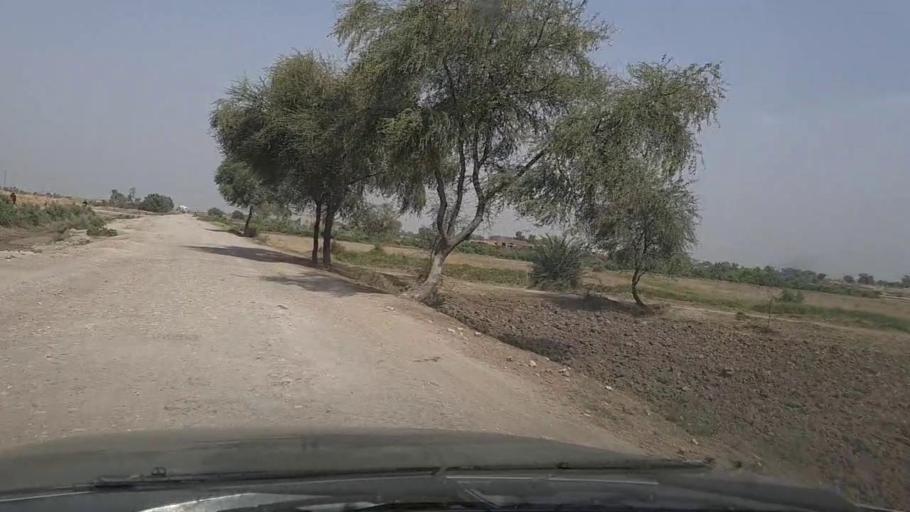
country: PK
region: Sindh
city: Thul
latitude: 28.4091
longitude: 68.6986
